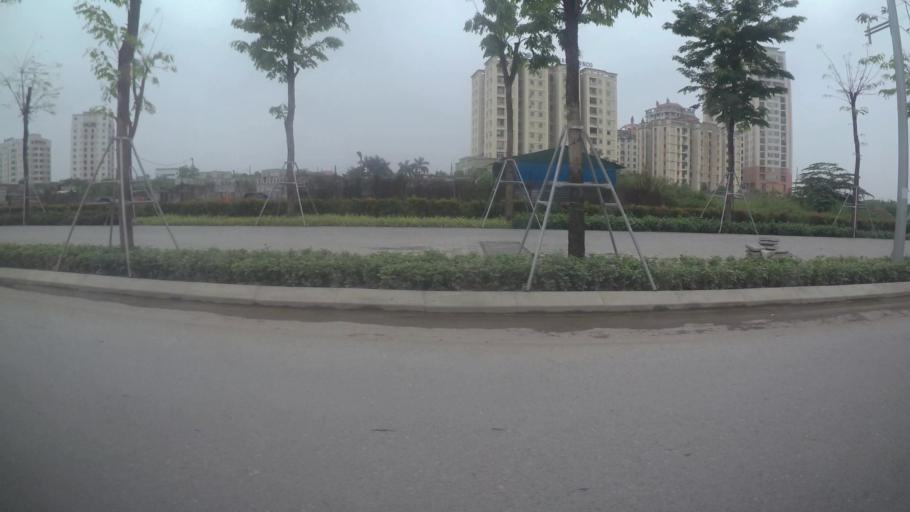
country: VN
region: Ha Noi
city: Tay Ho
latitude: 21.0663
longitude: 105.7847
